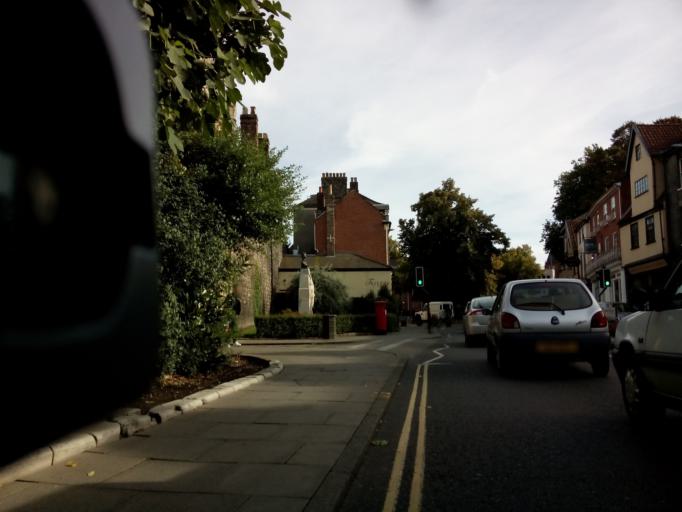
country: GB
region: England
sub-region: Norfolk
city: Norwich
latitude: 52.6318
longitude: 1.2989
